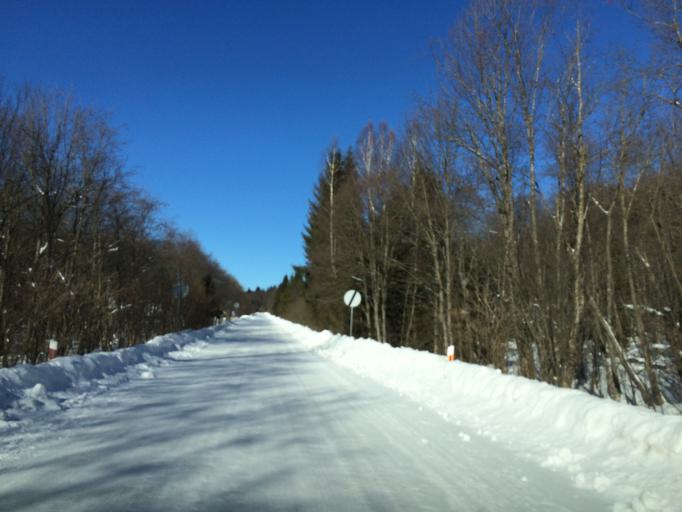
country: PL
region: Subcarpathian Voivodeship
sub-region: Powiat bieszczadzki
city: Lutowiska
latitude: 49.1075
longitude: 22.6283
